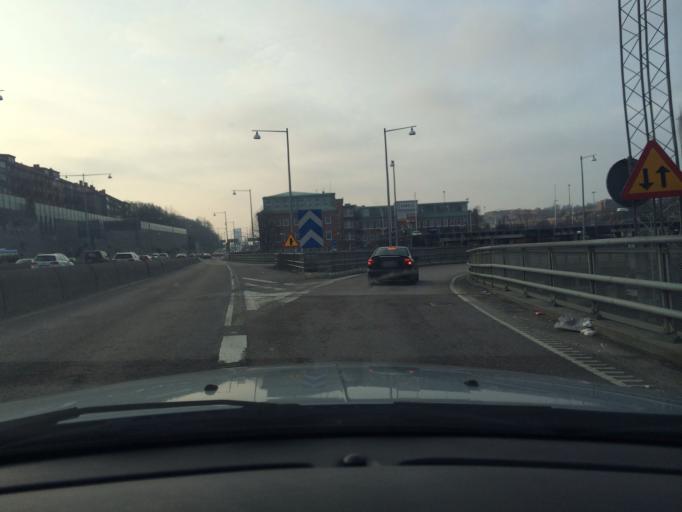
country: SE
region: Vaestra Goetaland
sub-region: Goteborg
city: Goeteborg
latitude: 57.6973
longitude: 11.9956
